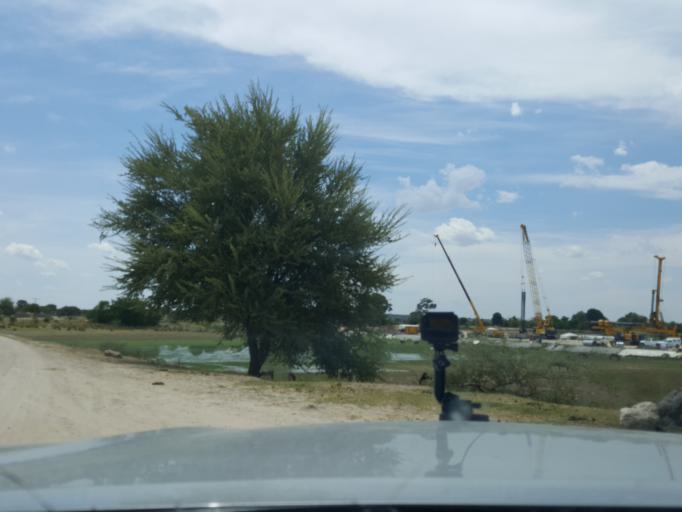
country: BW
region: North West
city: Shakawe
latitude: -18.2720
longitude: 21.7943
